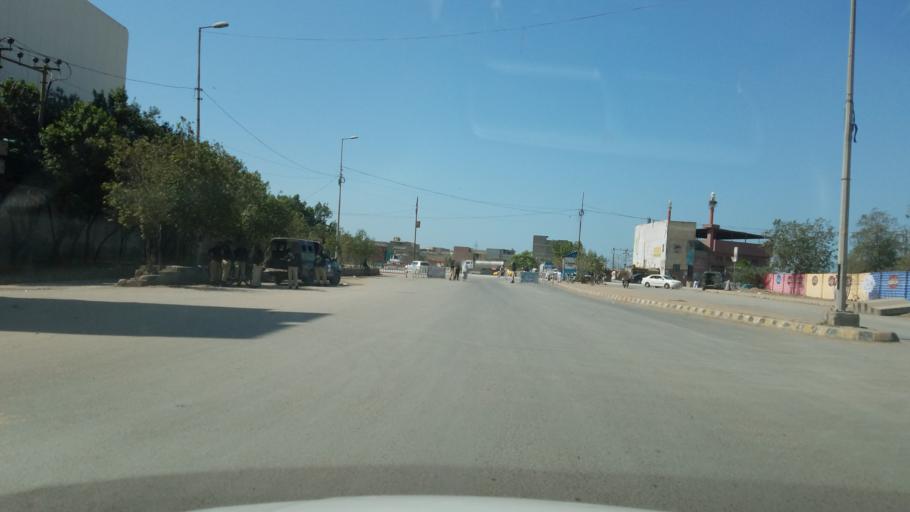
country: PK
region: Sindh
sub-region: Karachi District
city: Karachi
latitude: 24.8714
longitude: 66.9776
